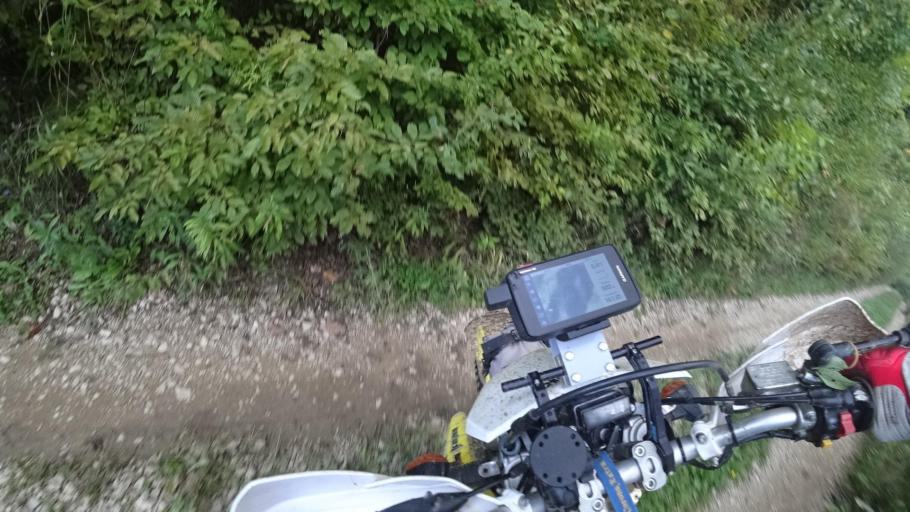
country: BA
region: Republika Srpska
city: Starcevica
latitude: 44.7062
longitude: 17.2219
